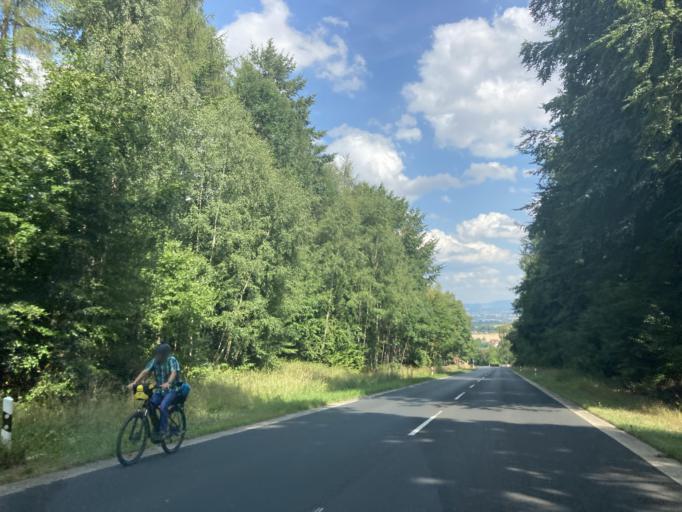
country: DE
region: Hesse
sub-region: Regierungsbezirk Kassel
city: Grossenluder
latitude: 50.5420
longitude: 9.5768
